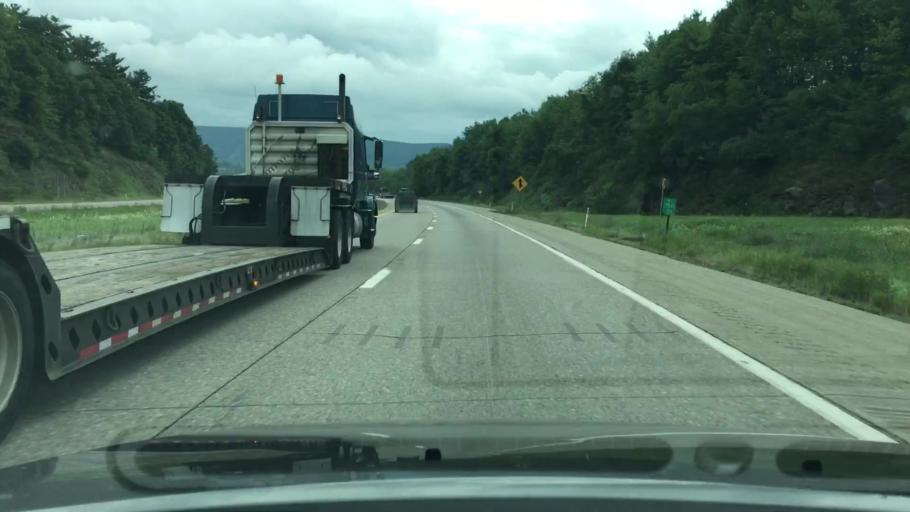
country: US
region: Pennsylvania
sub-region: Luzerne County
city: Conyngham
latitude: 41.0427
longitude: -76.0149
